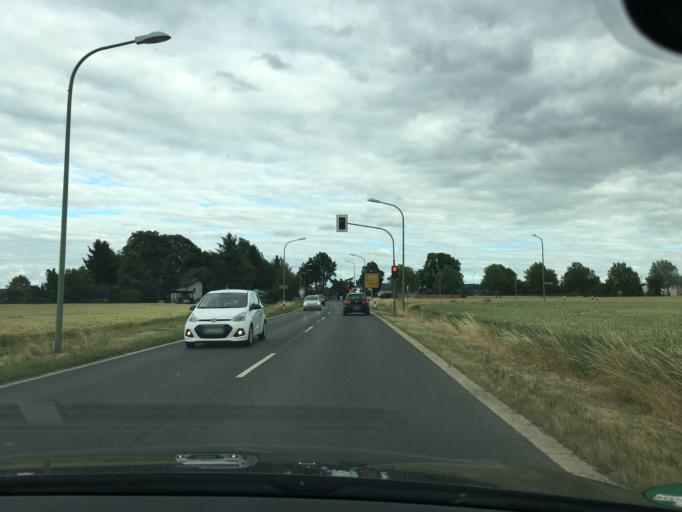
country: DE
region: North Rhine-Westphalia
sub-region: Regierungsbezirk Koln
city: Kreuzau
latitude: 50.7756
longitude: 6.4552
